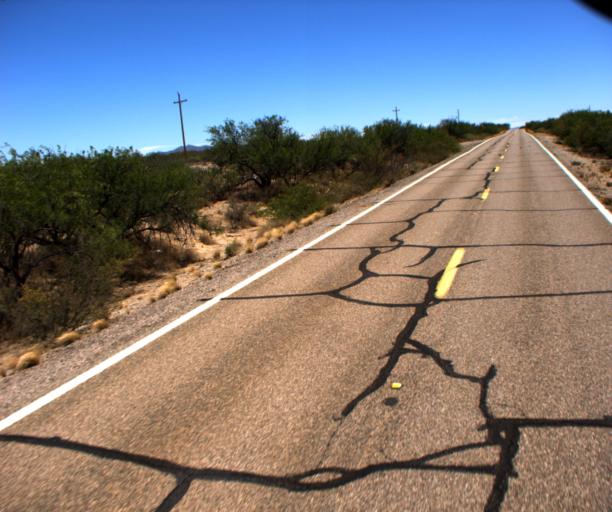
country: US
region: Arizona
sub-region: Pima County
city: Three Points
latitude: 31.9339
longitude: -111.3910
